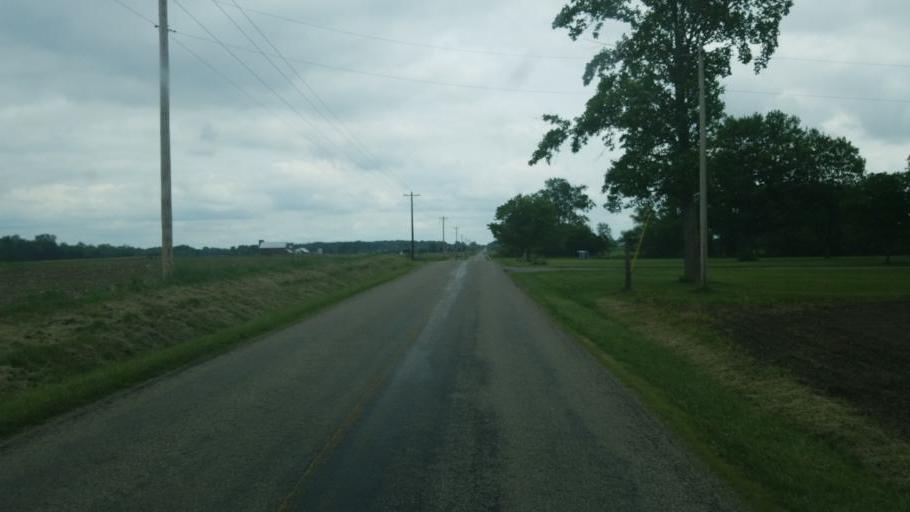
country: US
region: Ohio
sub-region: Fairfield County
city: Millersport
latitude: 39.8611
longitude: -82.5231
